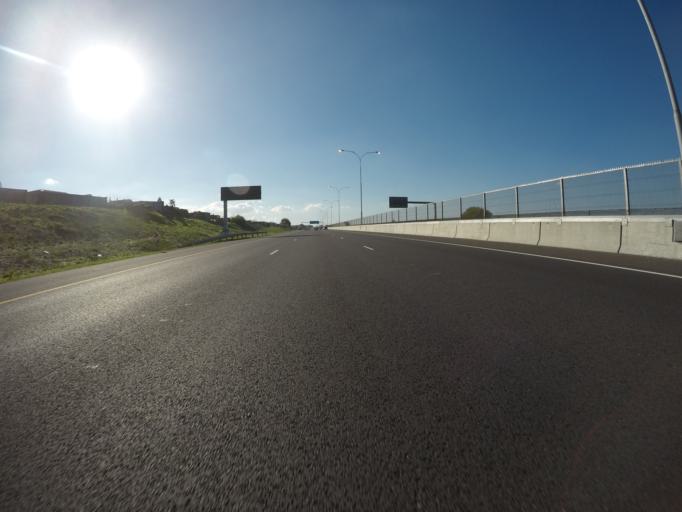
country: ZA
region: Western Cape
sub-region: City of Cape Town
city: Kraaifontein
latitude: -33.9664
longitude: 18.6549
